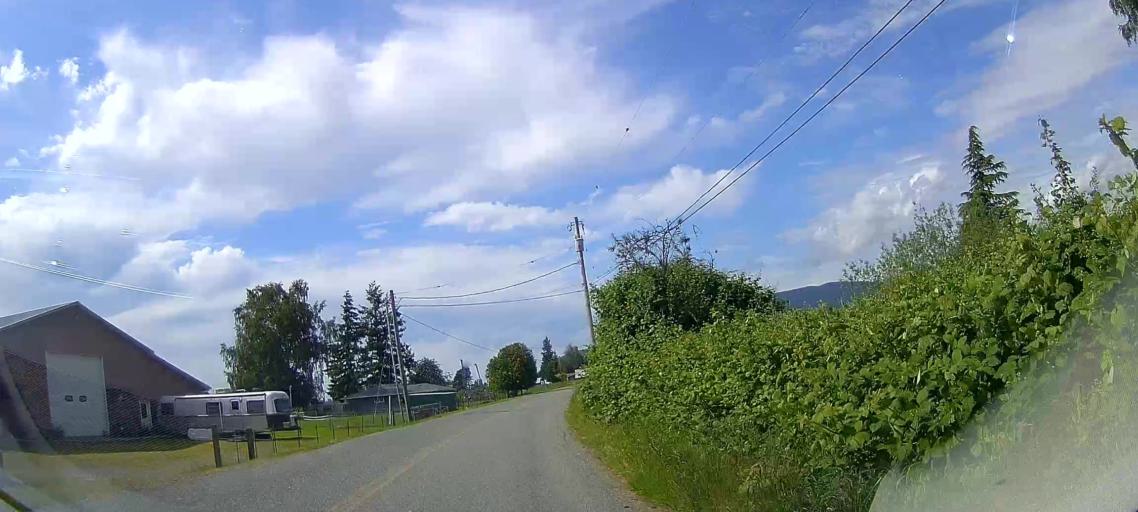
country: US
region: Washington
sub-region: Skagit County
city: Burlington
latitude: 48.5408
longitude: -122.3907
